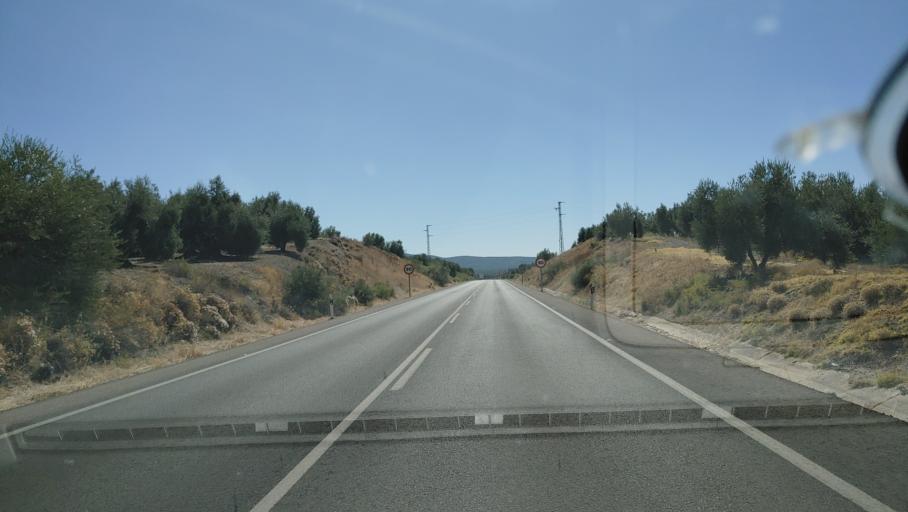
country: ES
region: Andalusia
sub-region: Provincia de Jaen
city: Campina
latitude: 38.2231
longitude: -2.9706
